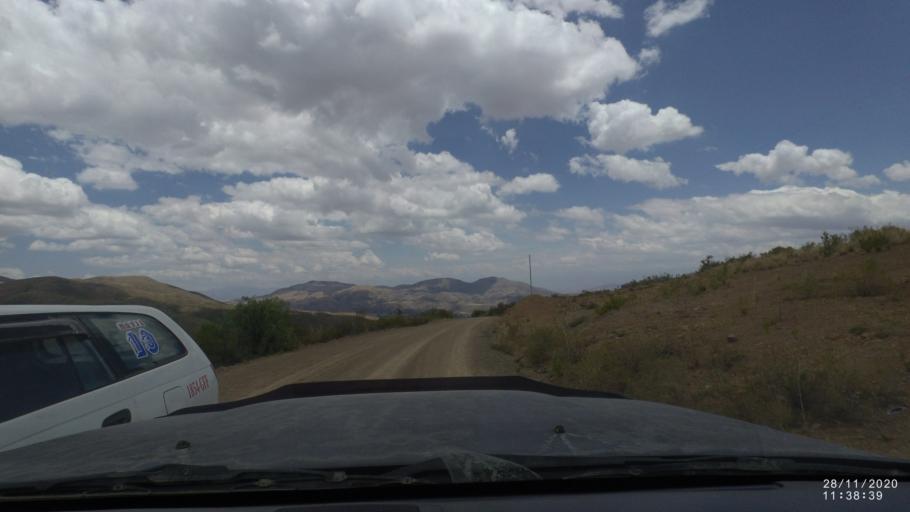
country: BO
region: Cochabamba
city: Tarata
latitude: -17.6773
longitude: -66.0441
